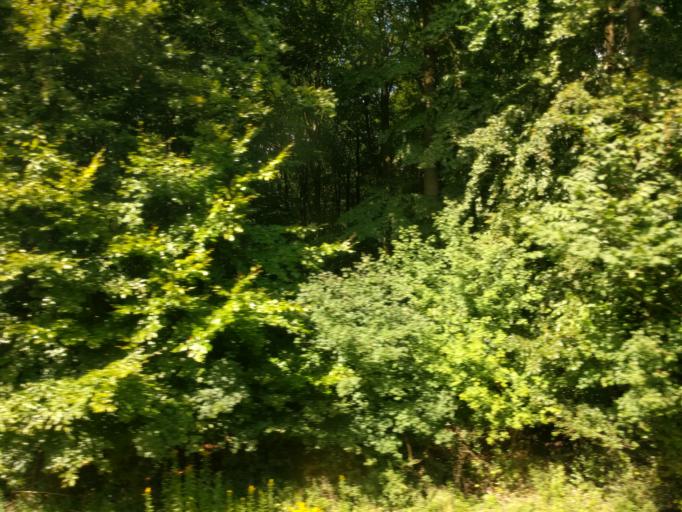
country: DK
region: Zealand
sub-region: Soro Kommune
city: Frederiksberg
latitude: 55.4221
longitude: 11.5843
